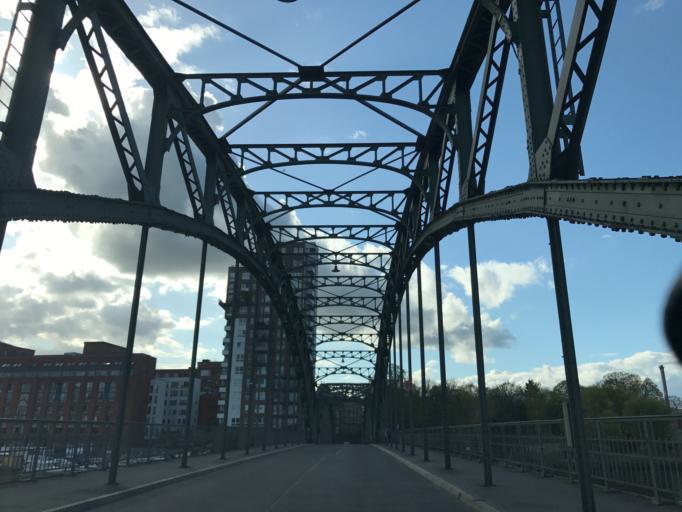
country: DE
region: Berlin
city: Hakenfelde
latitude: 52.5471
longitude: 13.2148
